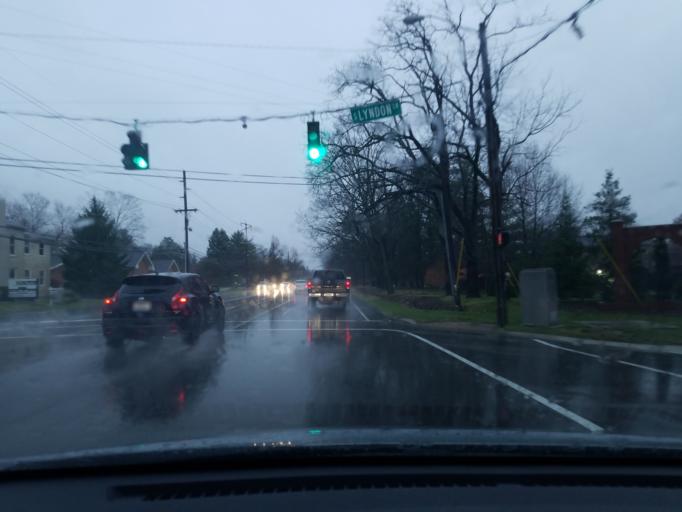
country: US
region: Kentucky
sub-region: Jefferson County
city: Lyndon
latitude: 38.2481
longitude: -85.5989
